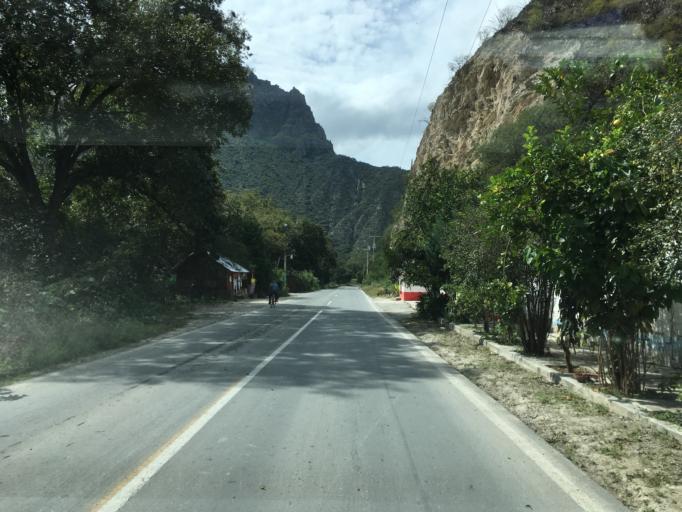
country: MX
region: Hidalgo
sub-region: San Agustin Metzquititlan
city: Mezquititlan
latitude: 20.5009
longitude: -98.6997
